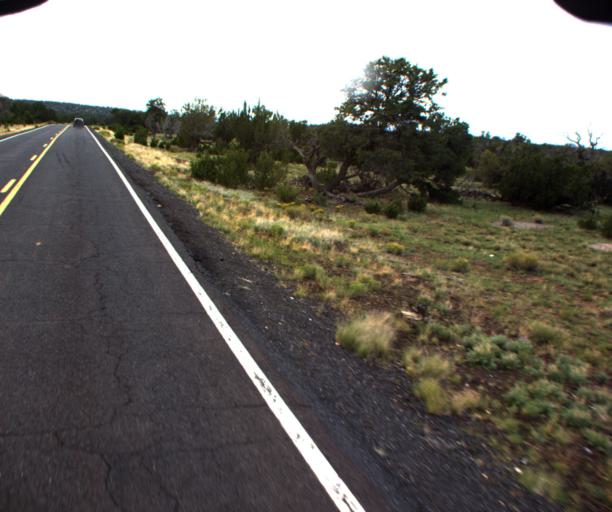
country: US
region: Arizona
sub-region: Coconino County
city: Parks
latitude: 35.5314
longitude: -111.8482
